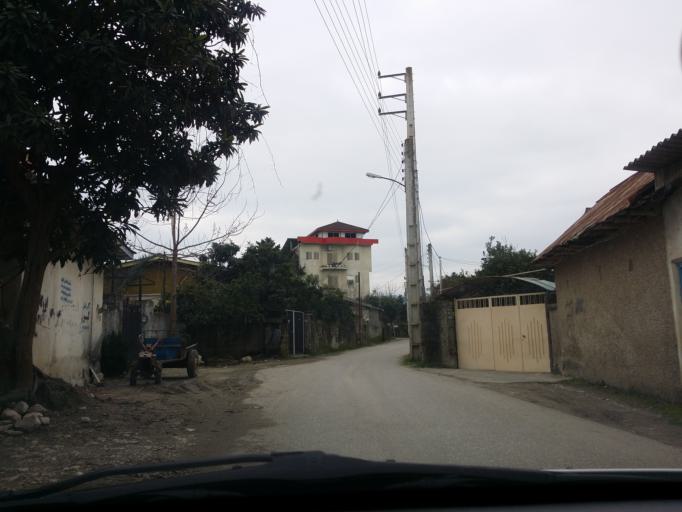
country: IR
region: Mazandaran
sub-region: Nowshahr
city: Nowshahr
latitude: 36.6469
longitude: 51.4759
